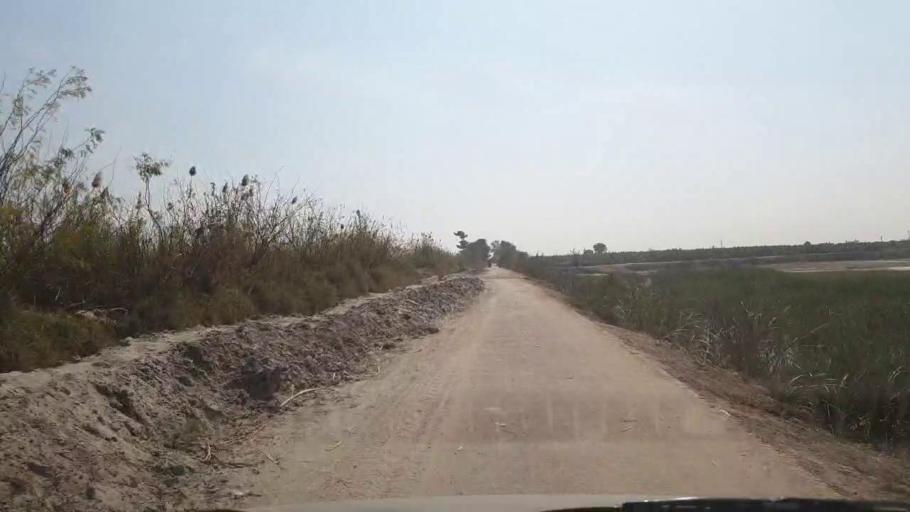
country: PK
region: Sindh
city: Chambar
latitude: 25.3577
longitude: 68.8218
